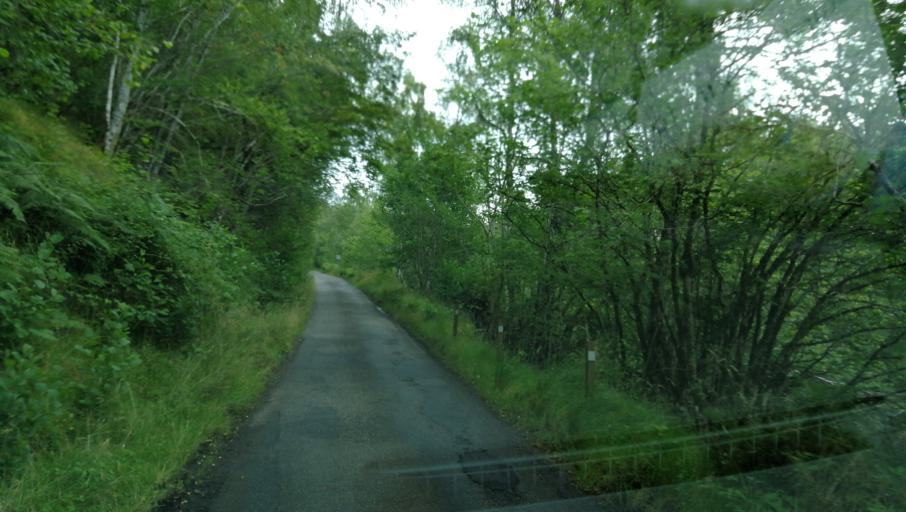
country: GB
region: Scotland
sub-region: Highland
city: Beauly
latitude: 57.3154
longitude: -4.8380
